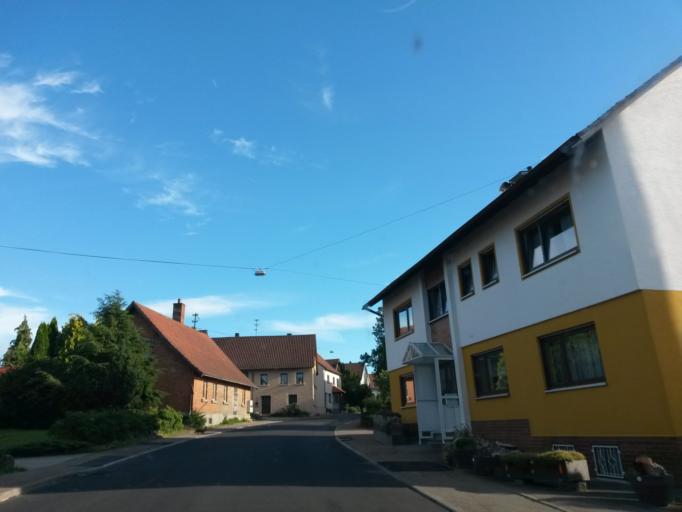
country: DE
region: Baden-Wuerttemberg
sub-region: Regierungsbezirk Stuttgart
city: Ellenberg
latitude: 49.0728
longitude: 10.2079
